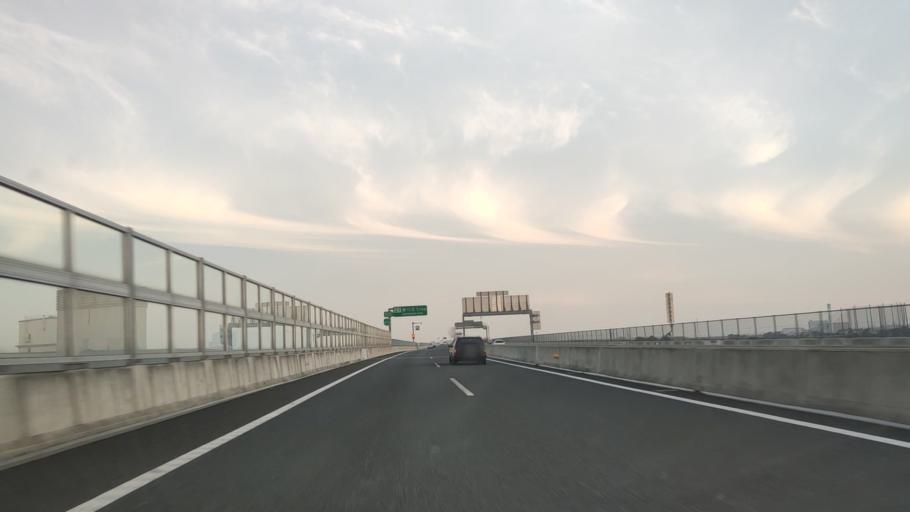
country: JP
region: Kanagawa
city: Atsugi
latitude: 35.4006
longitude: 139.3759
